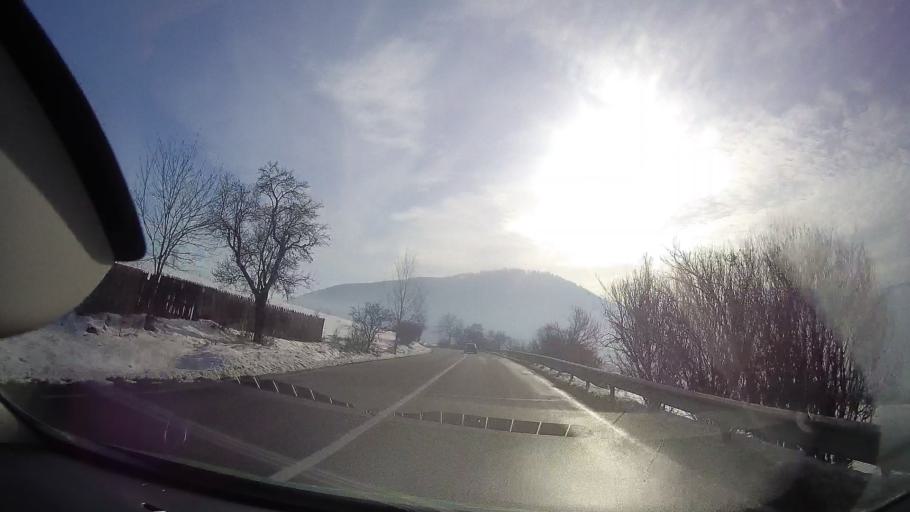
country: RO
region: Neamt
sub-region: Comuna Garcina
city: Garcina
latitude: 46.9819
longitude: 26.3582
